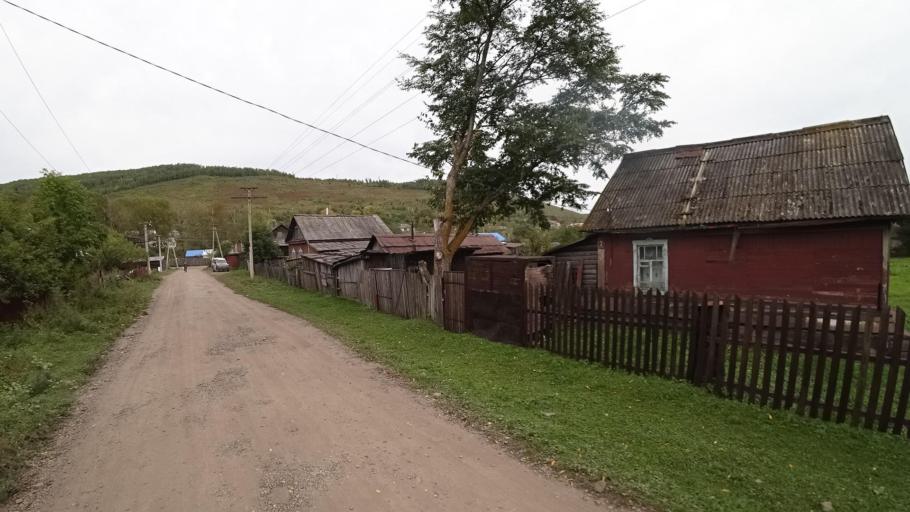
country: RU
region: Jewish Autonomous Oblast
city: Khingansk
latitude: 49.0335
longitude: 131.0549
